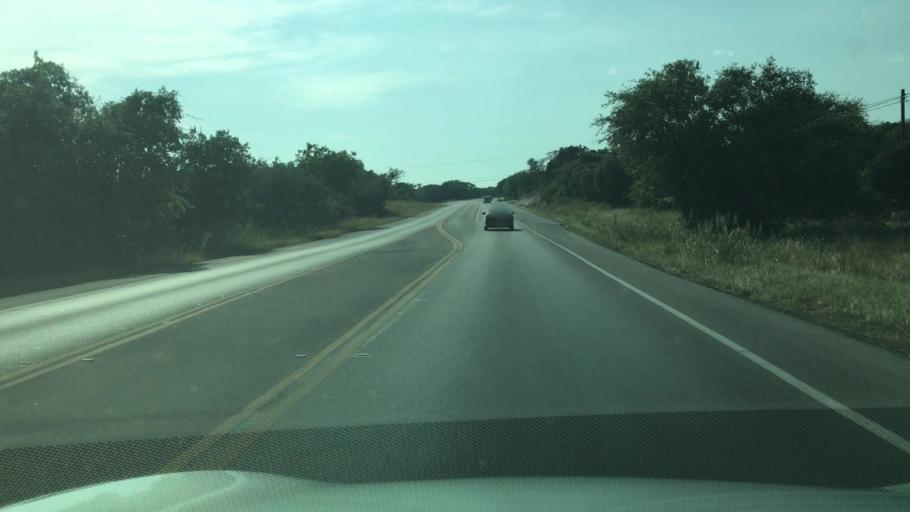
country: US
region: Texas
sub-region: Hays County
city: Wimberley
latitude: 29.9191
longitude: -98.0553
